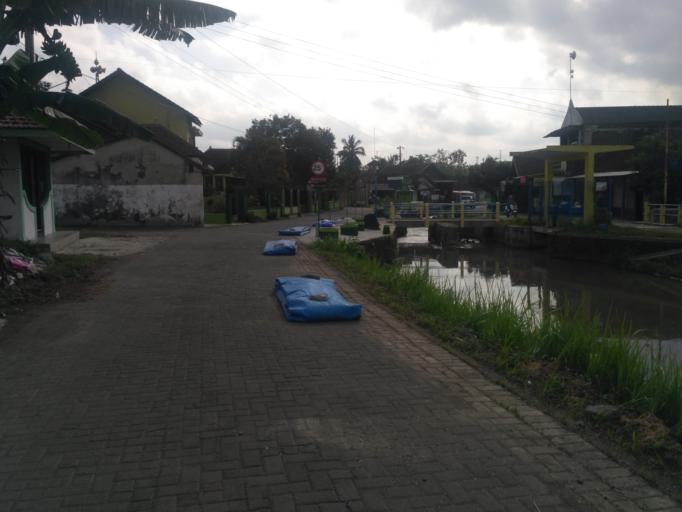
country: ID
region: Daerah Istimewa Yogyakarta
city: Melati
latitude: -7.7531
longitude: 110.3507
